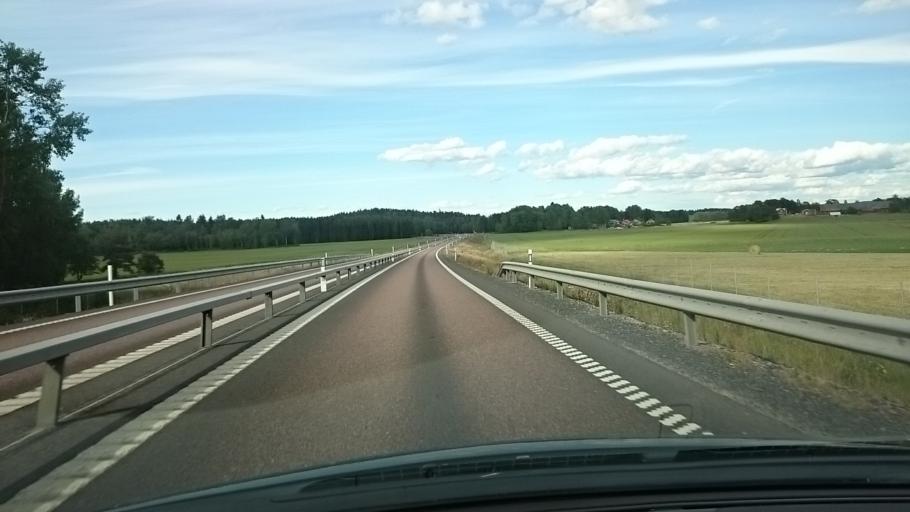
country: SE
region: OErebro
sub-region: Askersunds Kommun
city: Askersund
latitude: 58.8275
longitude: 14.8928
